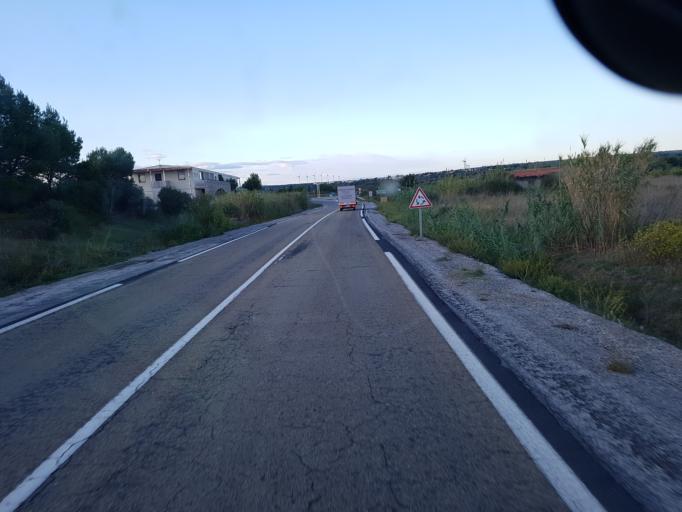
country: FR
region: Languedoc-Roussillon
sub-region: Departement de l'Aude
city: Leucate
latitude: 42.9570
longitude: 2.9852
